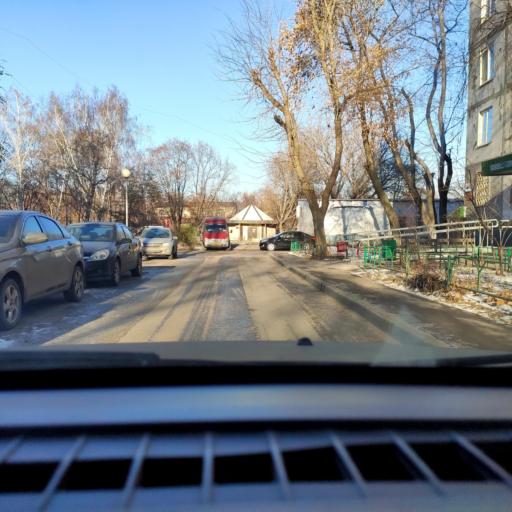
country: RU
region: Samara
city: Tol'yatti
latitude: 53.5148
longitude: 49.2672
